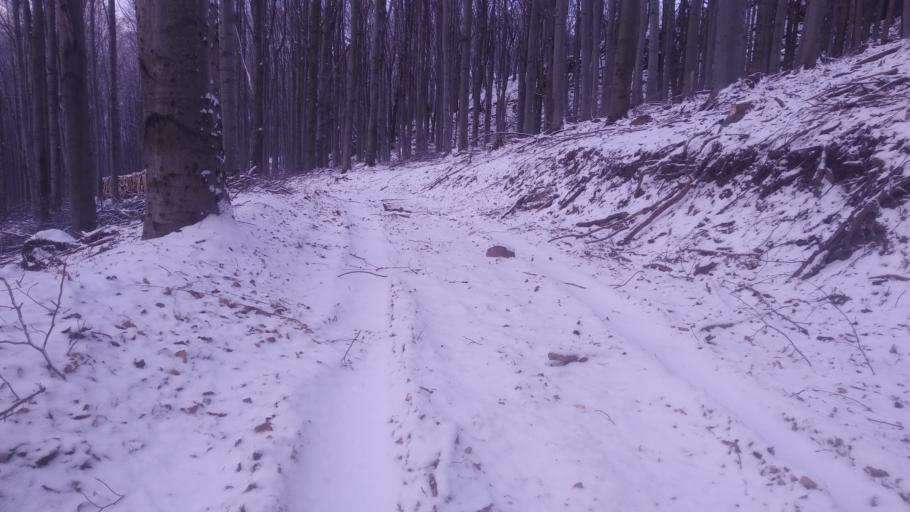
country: SK
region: Nitriansky
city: Sahy
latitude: 47.9698
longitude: 18.9302
